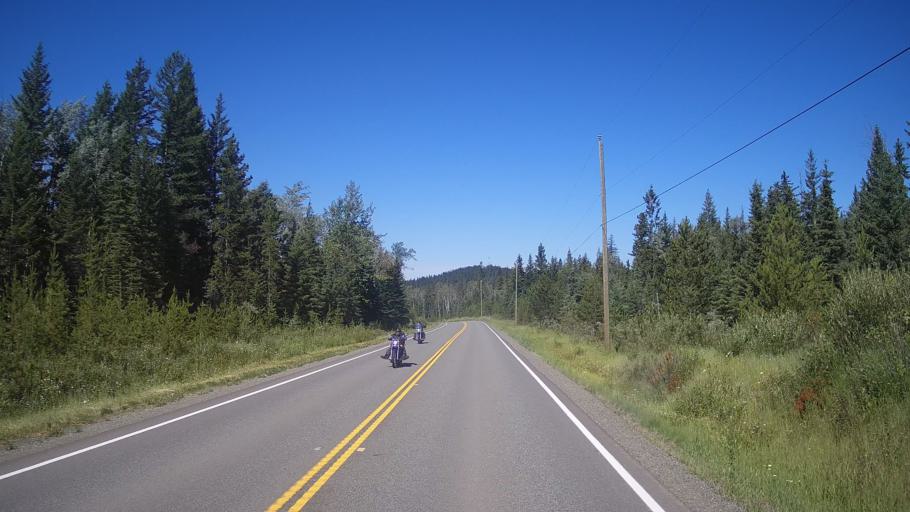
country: CA
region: British Columbia
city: Cache Creek
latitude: 51.5469
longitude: -121.0762
